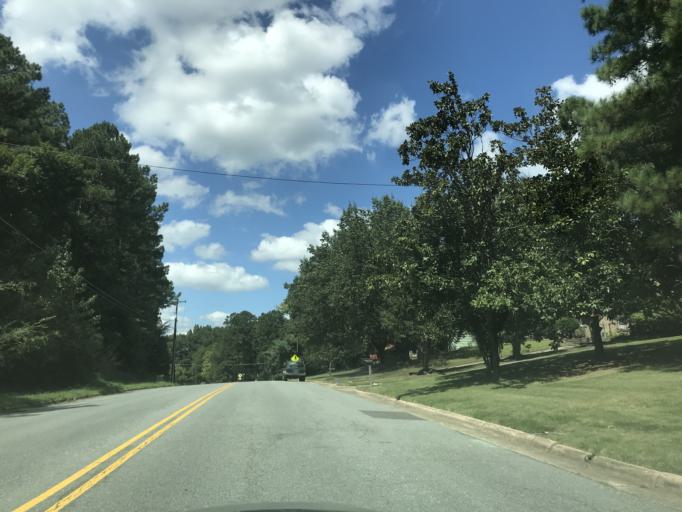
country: US
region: North Carolina
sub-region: Orange County
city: Chapel Hill
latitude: 35.9317
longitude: -79.0047
